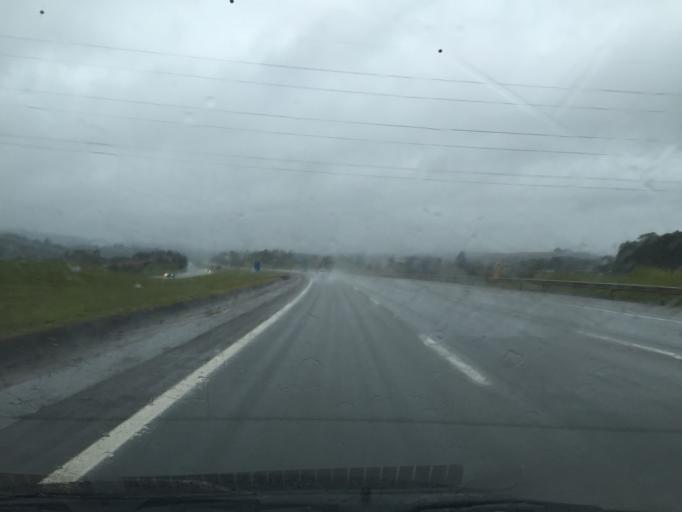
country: BR
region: Sao Paulo
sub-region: Mairinque
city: Mairinque
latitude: -23.4236
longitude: -47.2403
